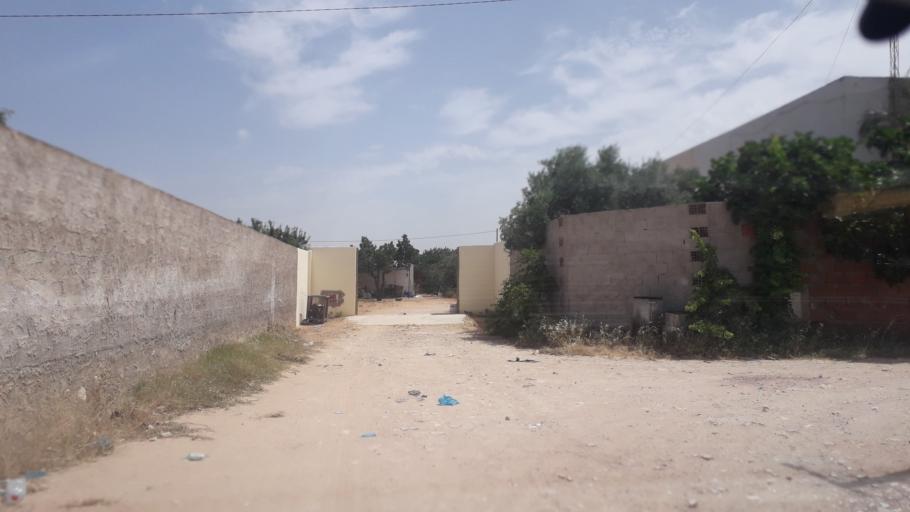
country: TN
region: Safaqis
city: Al Qarmadah
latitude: 34.8348
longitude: 10.7686
